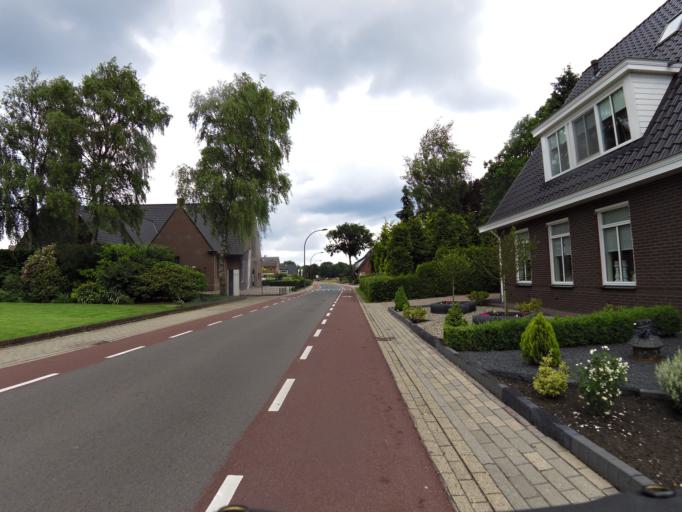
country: NL
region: Gelderland
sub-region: Gemeente Apeldoorn
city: Uddel
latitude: 52.2926
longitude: 5.7814
